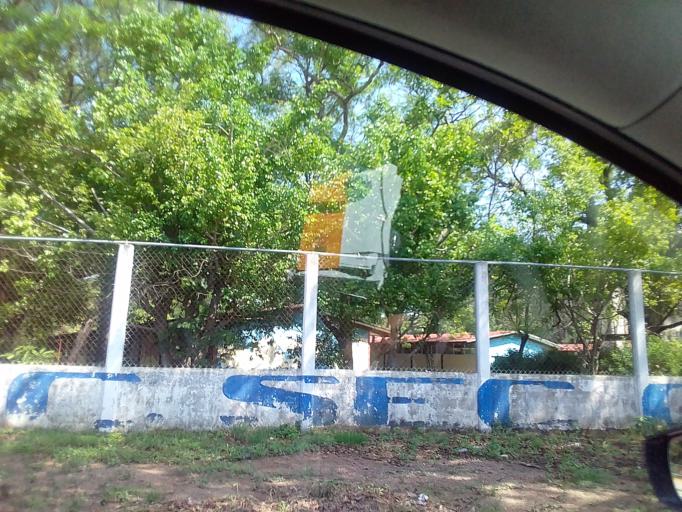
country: MX
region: Oaxaca
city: San Francisco Ixhuatan
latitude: 16.3585
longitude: -94.4798
